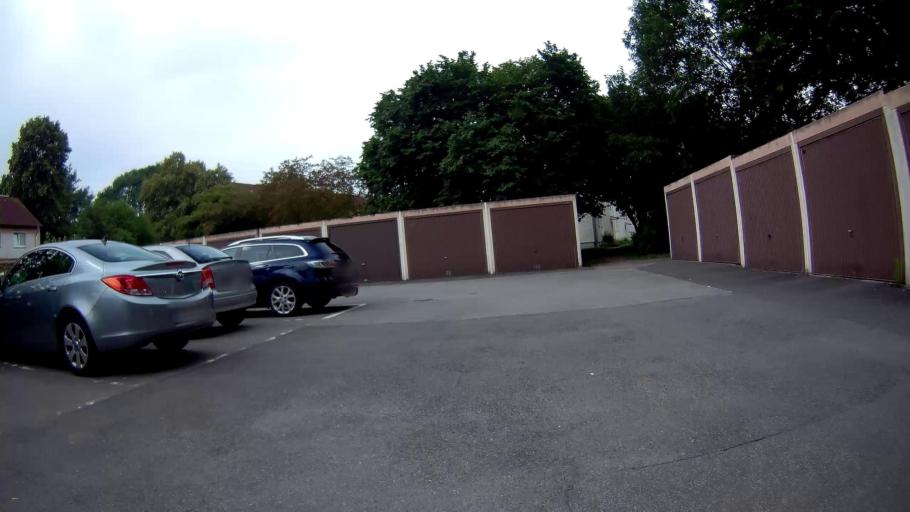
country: DE
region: North Rhine-Westphalia
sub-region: Regierungsbezirk Munster
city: Gladbeck
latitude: 51.5646
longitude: 7.0281
